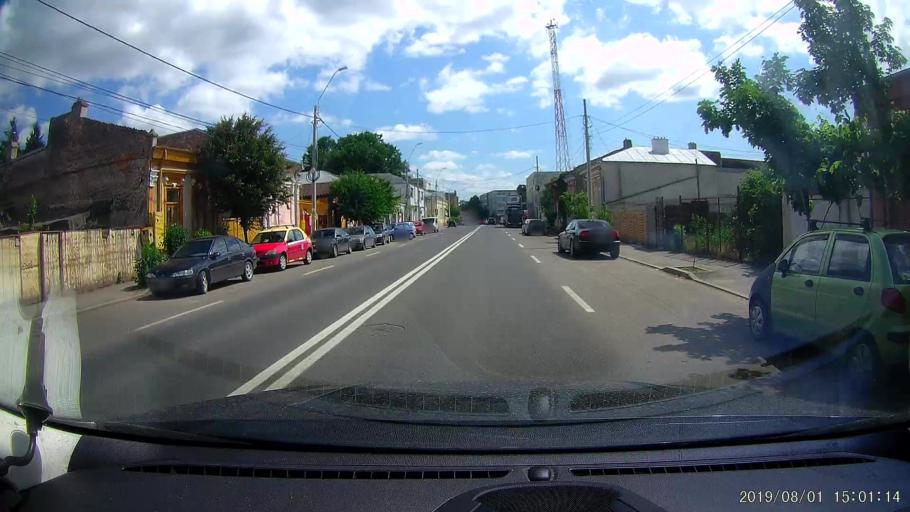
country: RO
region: Braila
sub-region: Municipiul Braila
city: Braila
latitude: 45.2733
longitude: 27.9606
